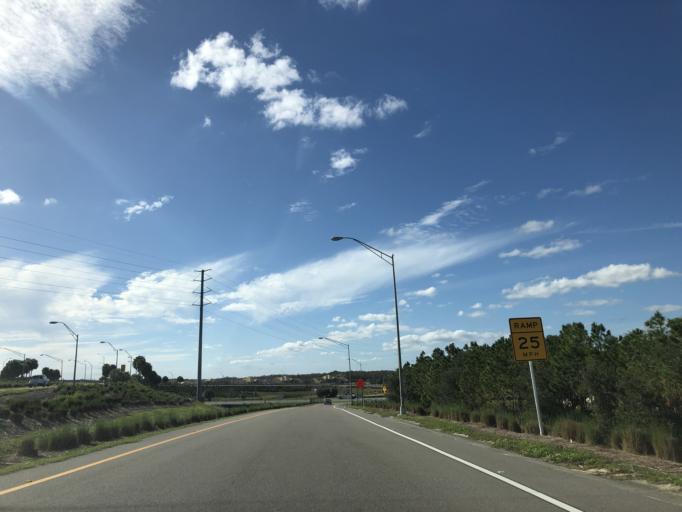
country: US
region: Florida
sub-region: Orange County
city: Hunters Creek
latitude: 28.3744
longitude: -81.4237
